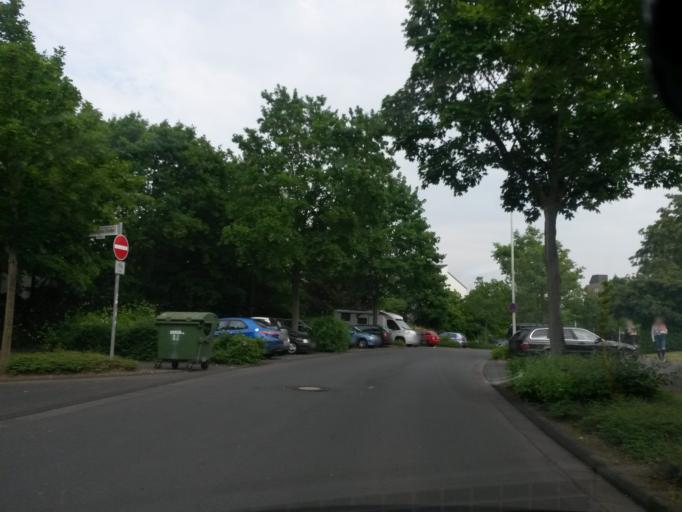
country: DE
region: North Rhine-Westphalia
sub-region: Regierungsbezirk Koln
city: Bonn
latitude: 50.7023
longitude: 7.0573
